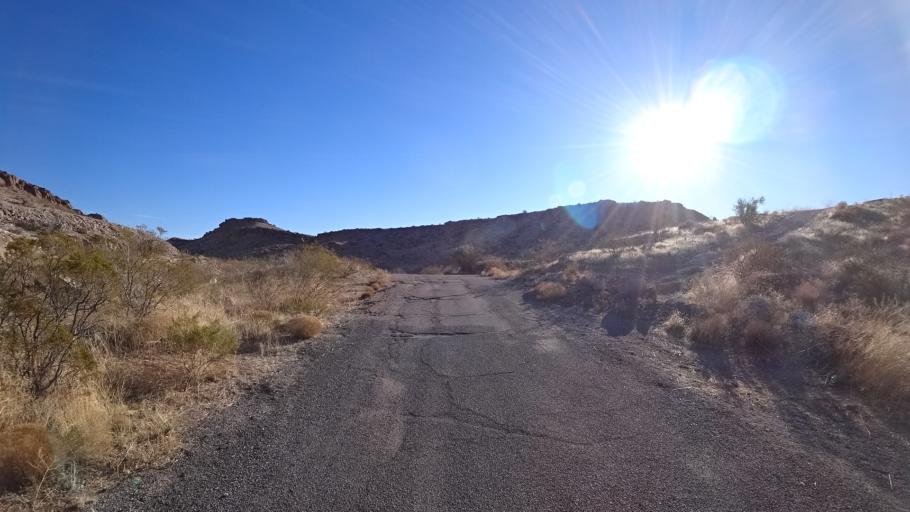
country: US
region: Arizona
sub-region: Mohave County
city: Kingman
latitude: 35.1842
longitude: -114.0354
